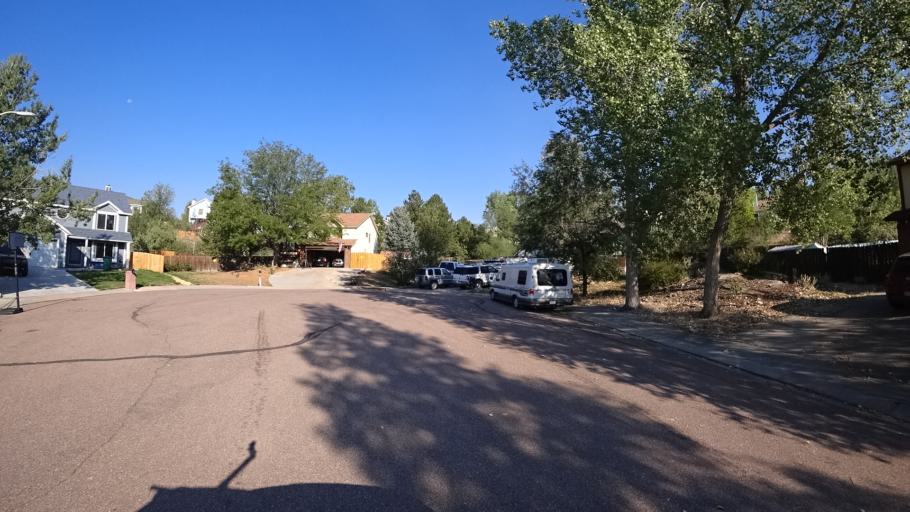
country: US
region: Colorado
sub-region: El Paso County
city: Stratmoor
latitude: 38.7784
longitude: -104.7997
